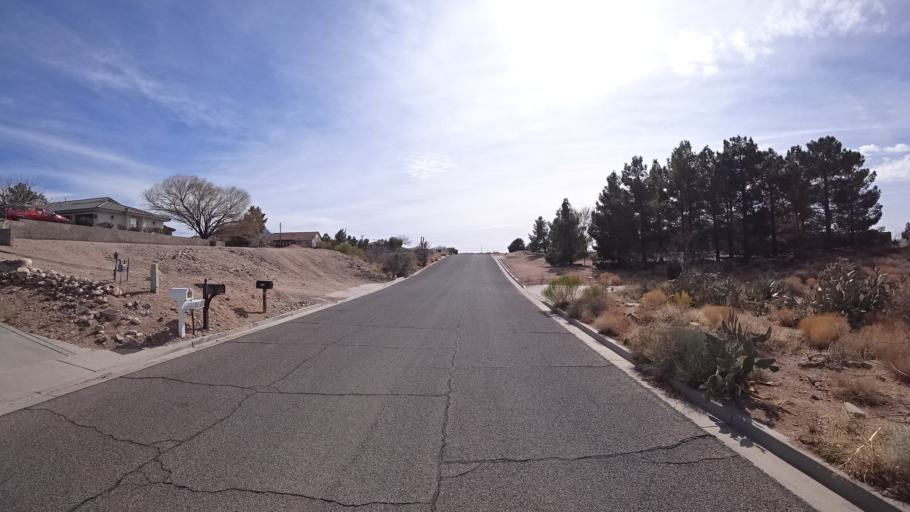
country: US
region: Arizona
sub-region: Mohave County
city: Kingman
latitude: 35.1830
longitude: -113.9860
